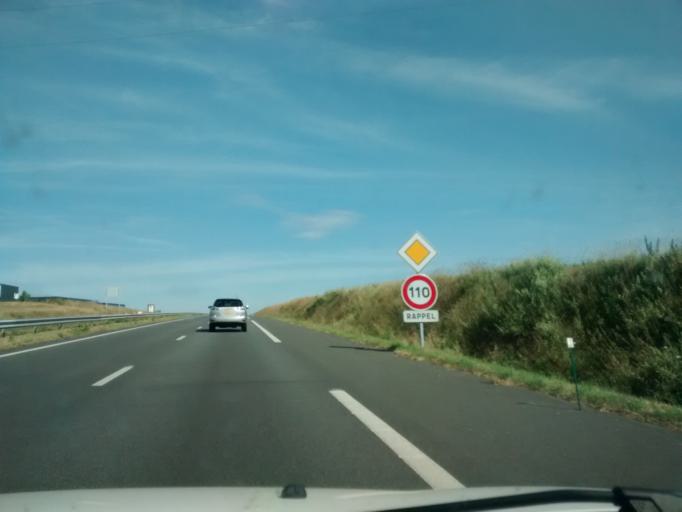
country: FR
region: Brittany
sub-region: Departement des Cotes-d'Armor
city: Sevignac
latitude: 48.3737
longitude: -2.3531
